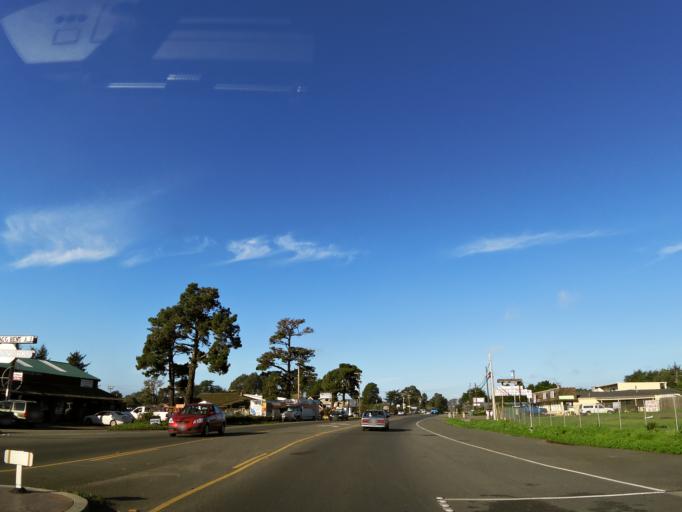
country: US
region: California
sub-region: Mendocino County
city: Fort Bragg
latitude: 39.4128
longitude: -123.8083
